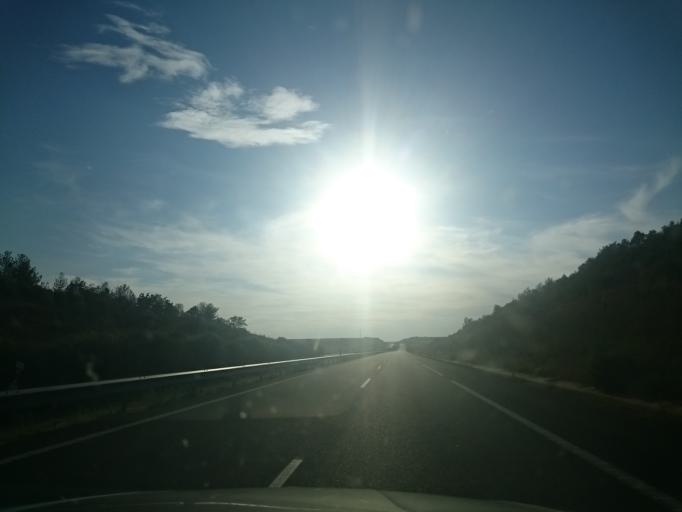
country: ES
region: Castille and Leon
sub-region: Provincia de Palencia
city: Ledigos
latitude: 42.3620
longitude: -4.8462
